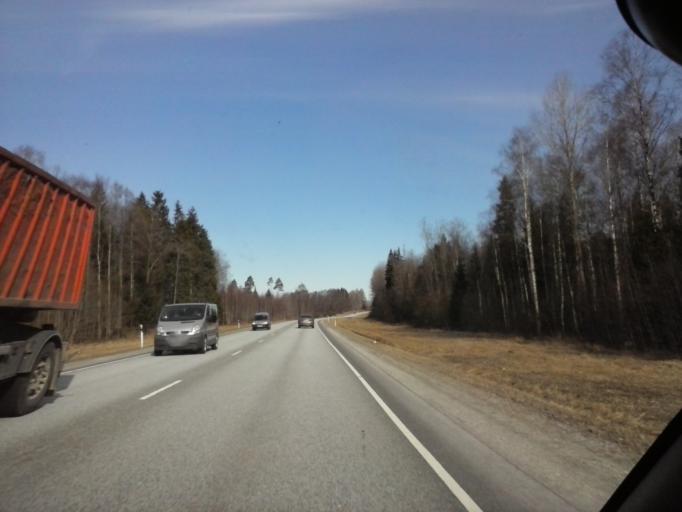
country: EE
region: Jaervamaa
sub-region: Paide linn
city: Paide
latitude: 59.0479
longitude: 25.4352
